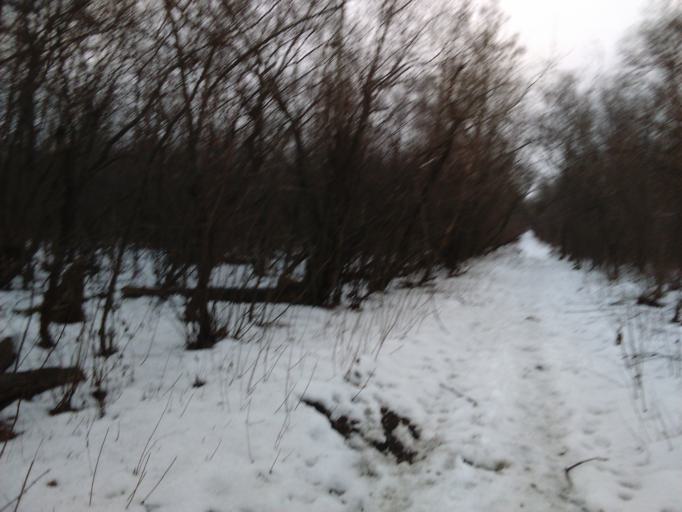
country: RU
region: Rostov
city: Temernik
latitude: 47.3506
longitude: 39.7395
